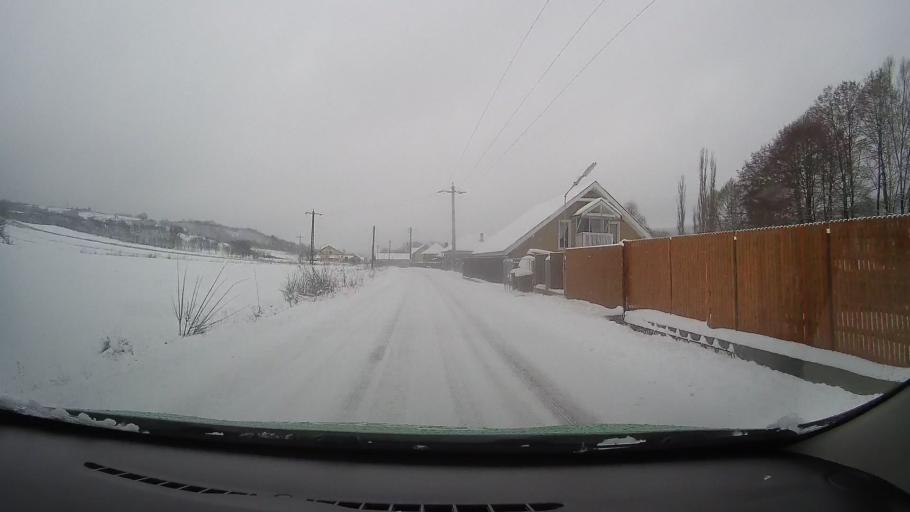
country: RO
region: Hunedoara
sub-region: Comuna Carjiti
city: Carjiti
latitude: 45.8308
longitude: 22.8431
